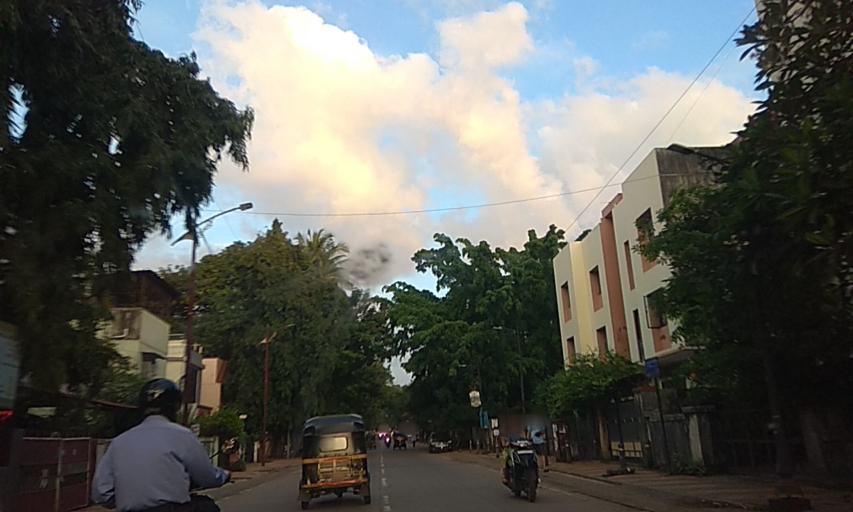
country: IN
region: Maharashtra
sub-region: Pune Division
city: Pune
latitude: 18.4927
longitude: 73.8518
